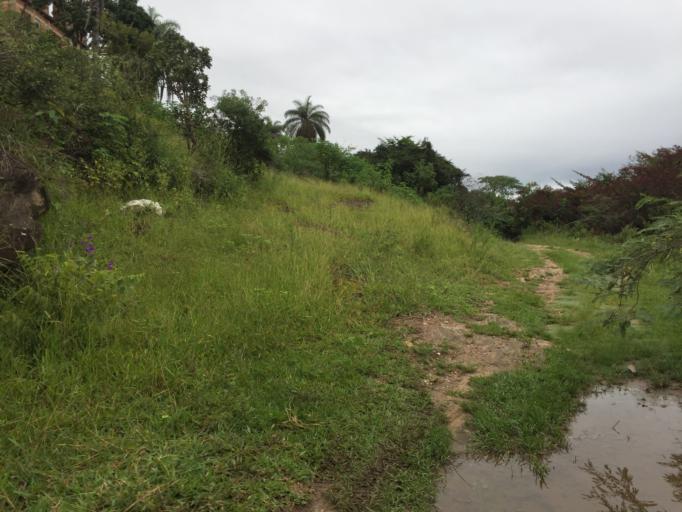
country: BR
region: Minas Gerais
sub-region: Sao Joao Del Rei
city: Sao Joao del Rei
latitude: -21.1285
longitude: -44.2683
